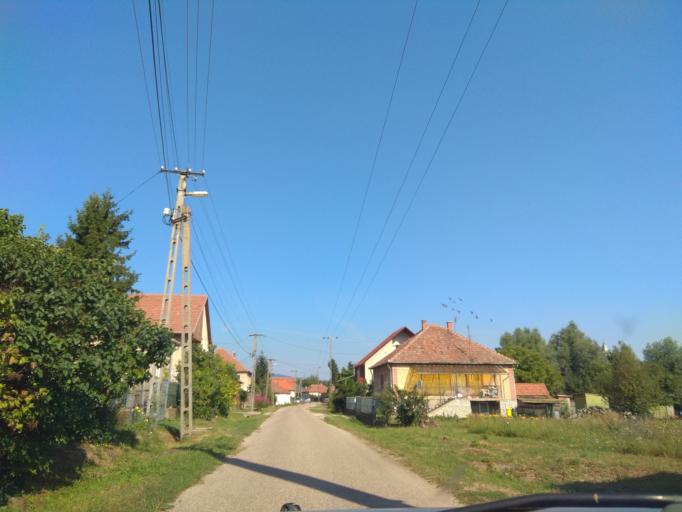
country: HU
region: Borsod-Abauj-Zemplen
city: Harsany
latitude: 47.9823
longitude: 20.7840
